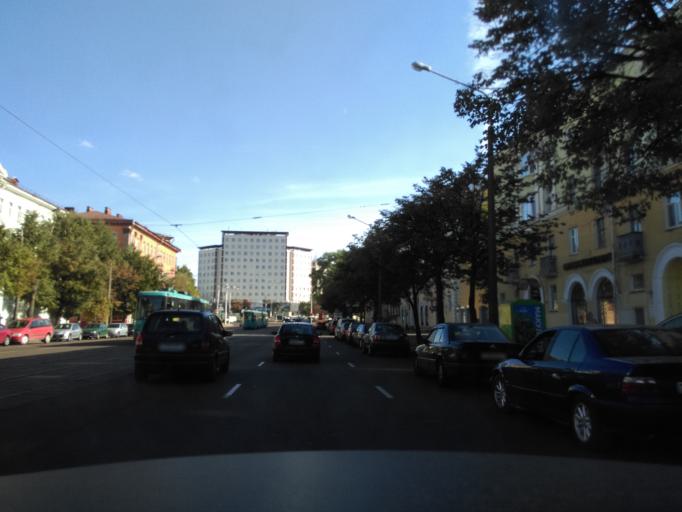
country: BY
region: Minsk
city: Minsk
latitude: 53.9061
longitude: 27.5837
